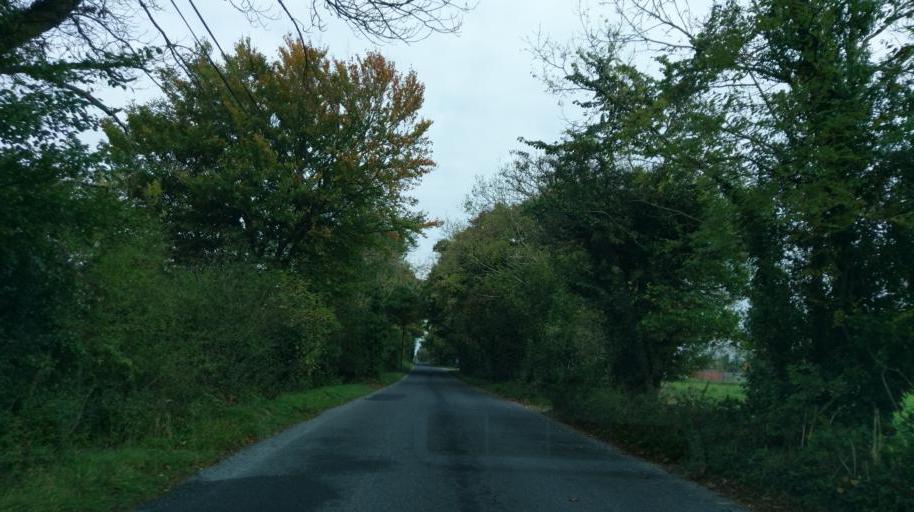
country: IE
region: Connaught
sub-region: County Galway
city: Athenry
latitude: 53.4360
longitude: -8.6380
